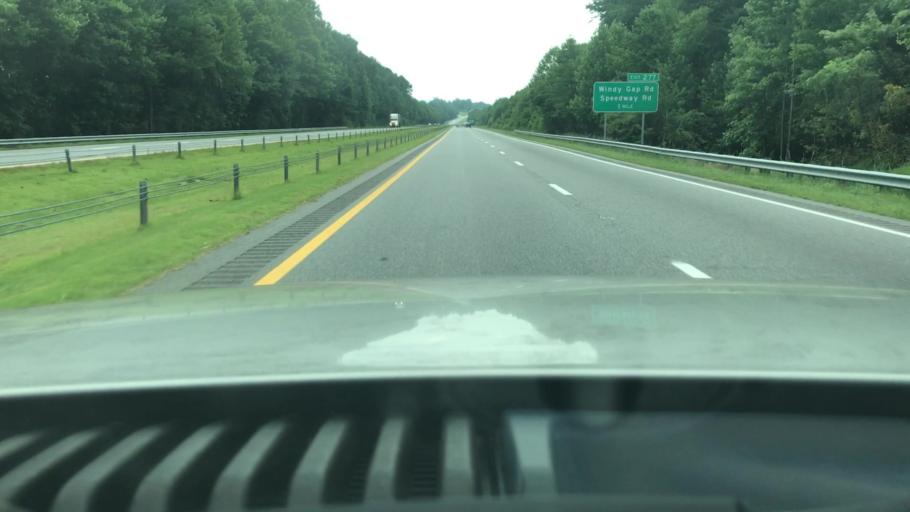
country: US
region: North Carolina
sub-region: Wilkes County
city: North Wilkesboro
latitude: 36.1476
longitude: -81.0389
